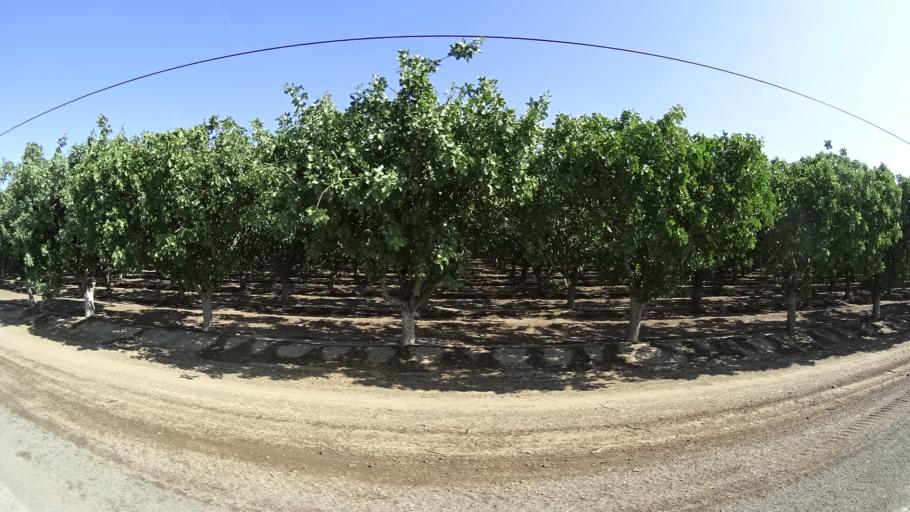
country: US
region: California
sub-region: Kings County
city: Home Garden
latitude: 36.2550
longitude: -119.5587
